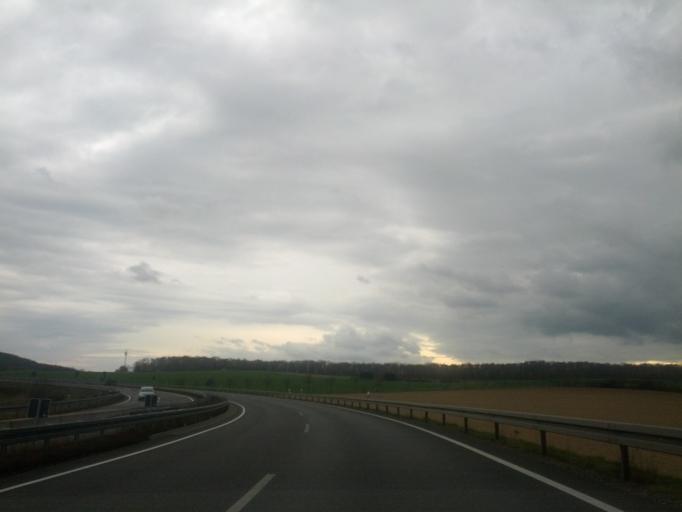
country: DE
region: Lower Saxony
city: Rosdorf
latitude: 51.4571
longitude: 9.8640
